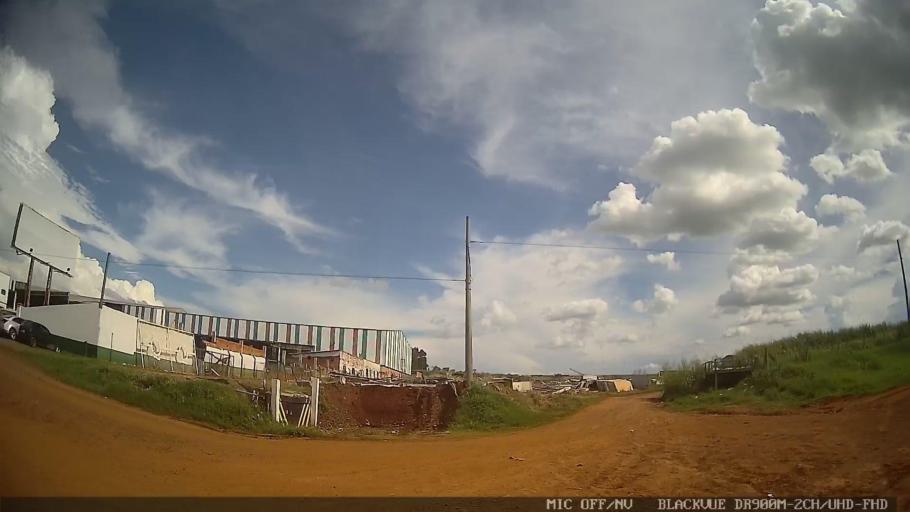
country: BR
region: Sao Paulo
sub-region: Laranjal Paulista
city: Laranjal Paulista
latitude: -23.0419
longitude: -47.9063
